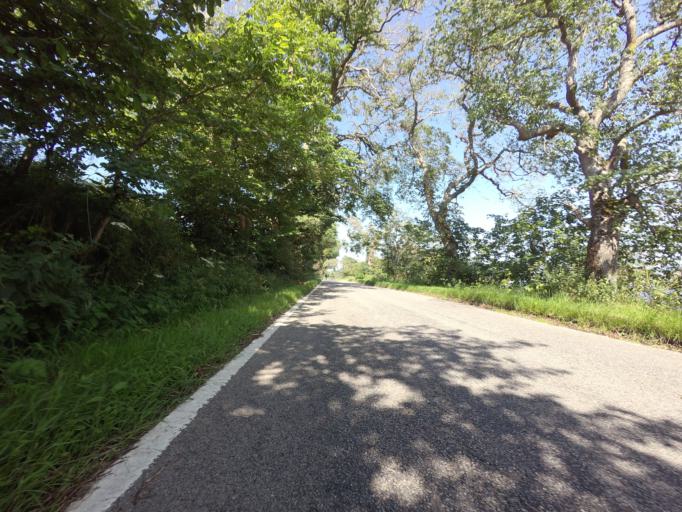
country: GB
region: Scotland
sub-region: Highland
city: Dingwall
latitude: 57.6177
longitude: -4.4048
